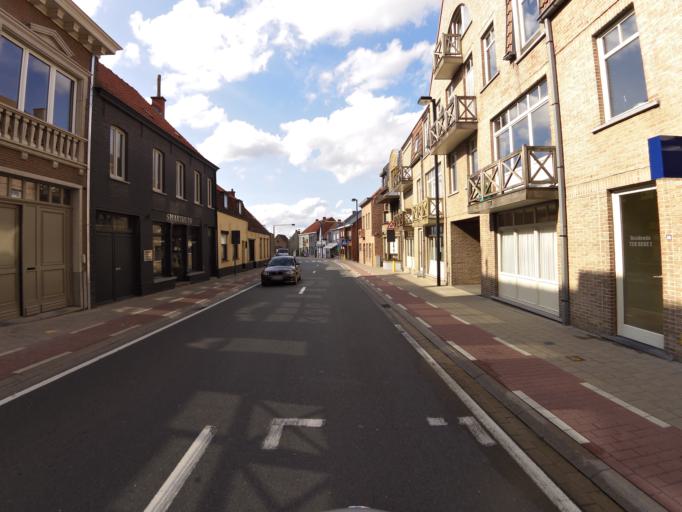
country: BE
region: Flanders
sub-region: Provincie West-Vlaanderen
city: Anzegem
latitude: 50.8367
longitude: 3.4762
